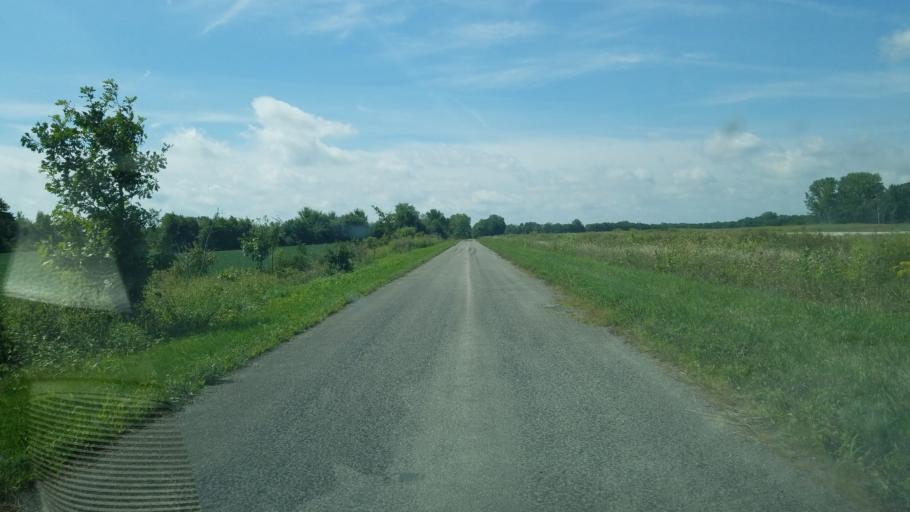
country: US
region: Ohio
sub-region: Hardin County
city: Kenton
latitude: 40.6069
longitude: -83.6464
